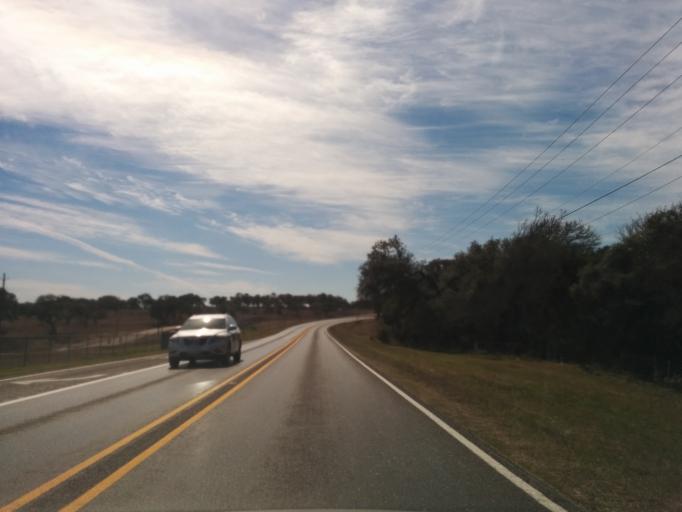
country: US
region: Texas
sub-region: Bexar County
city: Fair Oaks Ranch
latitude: 29.7109
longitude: -98.6280
